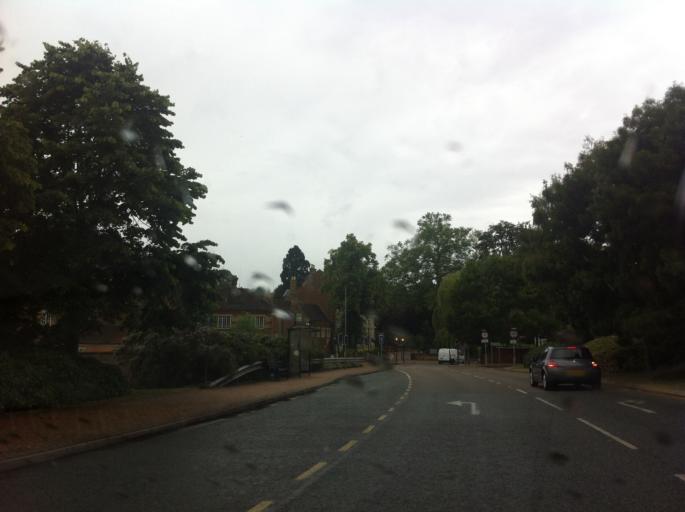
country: GB
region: England
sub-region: Northamptonshire
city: Wellingborough
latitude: 52.3001
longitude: -0.6899
